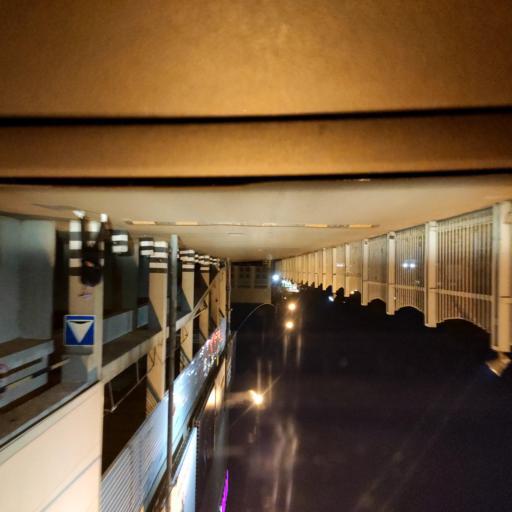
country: RU
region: Moscow
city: Leonovo
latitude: 55.8460
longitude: 37.6588
